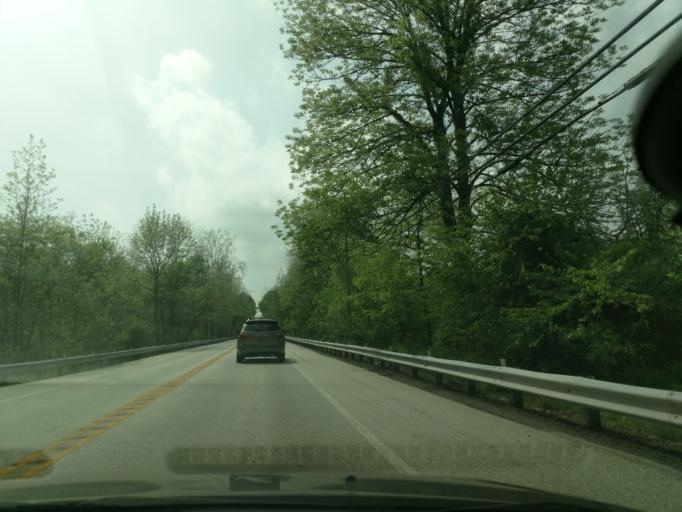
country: US
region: Pennsylvania
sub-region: Chester County
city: South Pottstown
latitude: 40.1733
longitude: -75.6932
